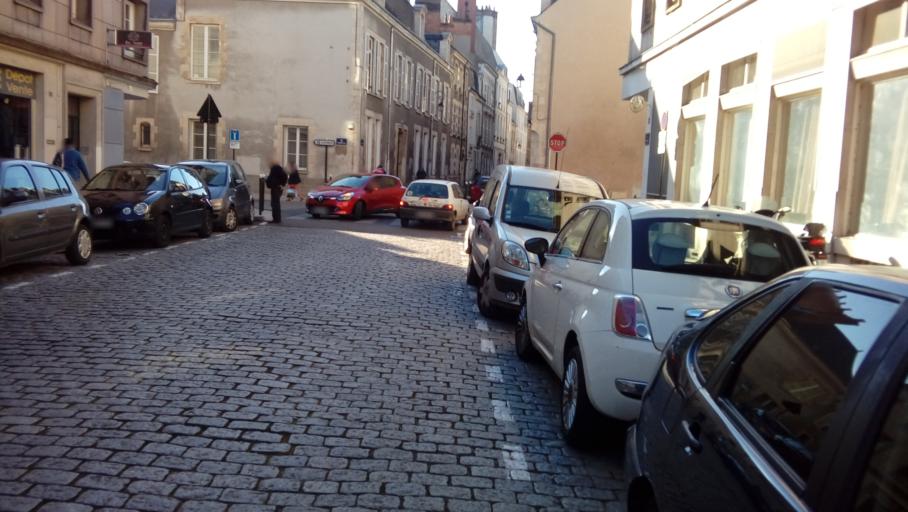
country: FR
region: Centre
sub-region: Departement du Loiret
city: Orleans
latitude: 47.9025
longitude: 1.9016
